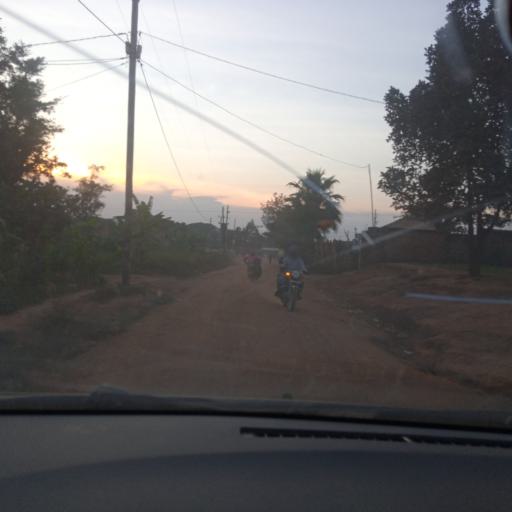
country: UG
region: Central Region
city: Masaka
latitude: -0.3105
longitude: 31.7645
